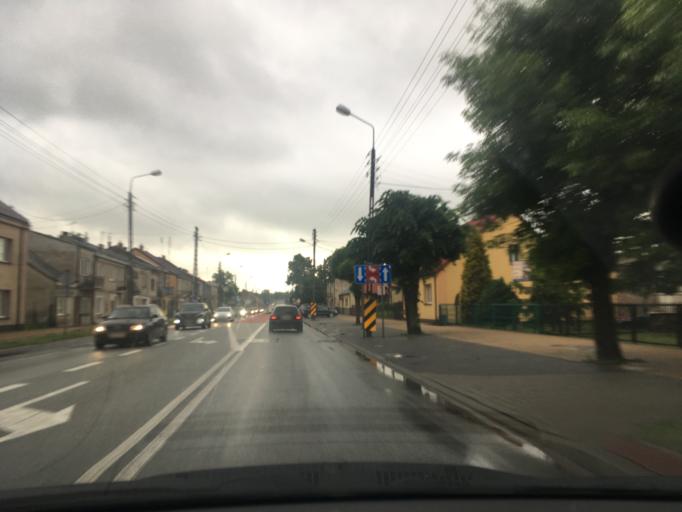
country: PL
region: Lublin Voivodeship
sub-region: Powiat rycki
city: Deblin
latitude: 51.5608
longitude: 21.8568
